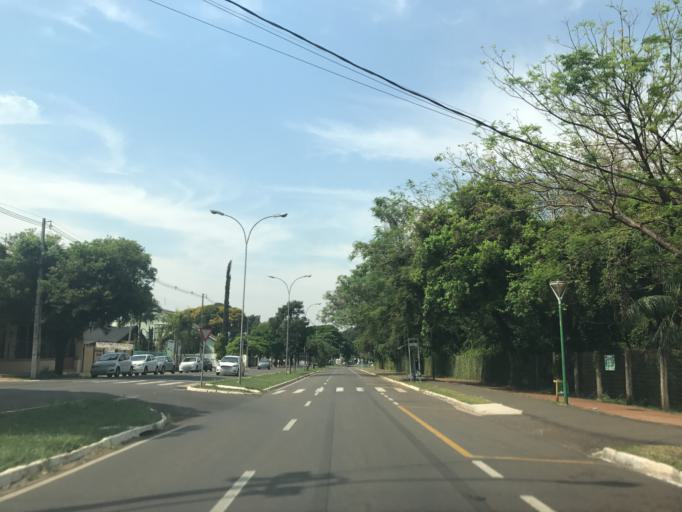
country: BR
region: Parana
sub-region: Maringa
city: Maringa
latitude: -23.4295
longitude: -51.9417
